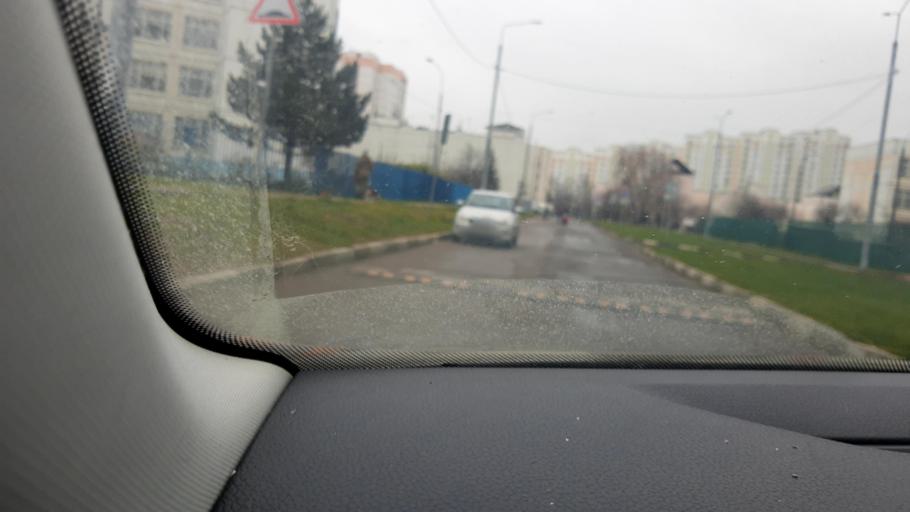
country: RU
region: Moskovskaya
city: Shcherbinka
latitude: 55.5480
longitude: 37.5624
